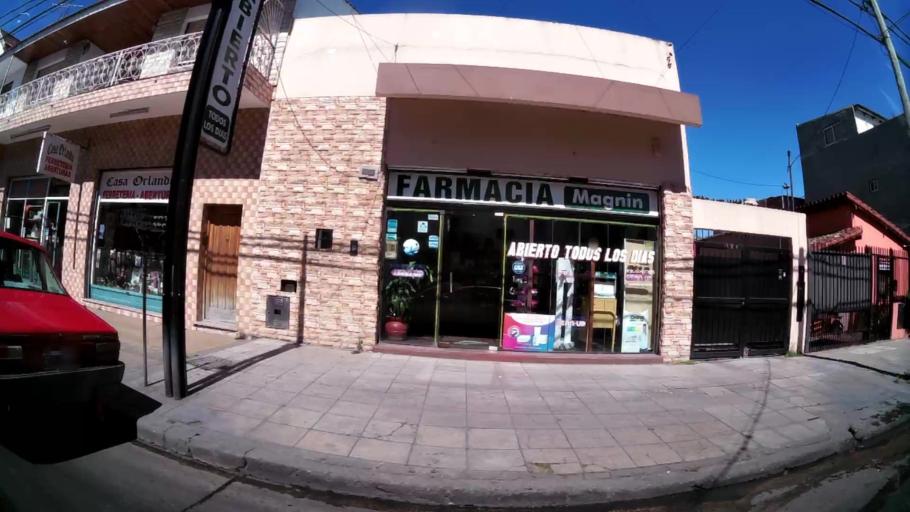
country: AR
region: Buenos Aires
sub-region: Partido de Tigre
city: Tigre
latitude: -34.4907
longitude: -58.6130
